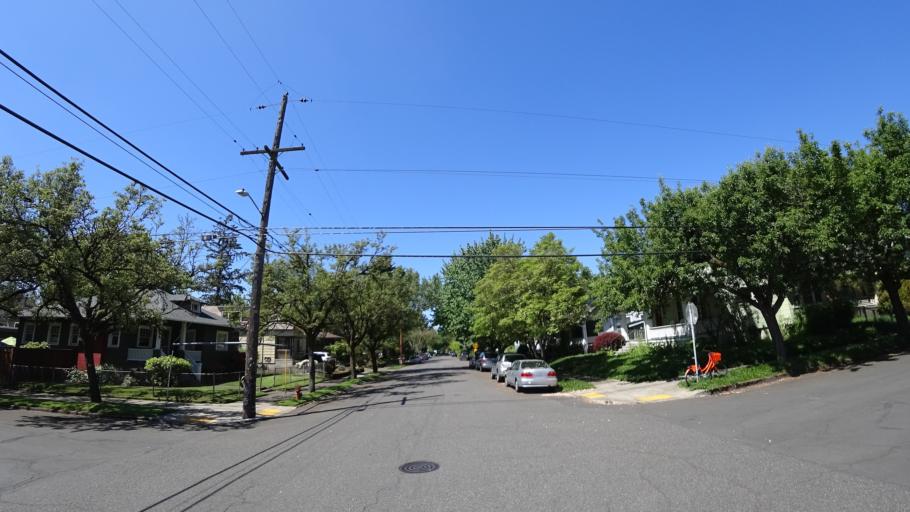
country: US
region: Oregon
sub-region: Multnomah County
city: Portland
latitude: 45.5088
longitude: -122.6239
